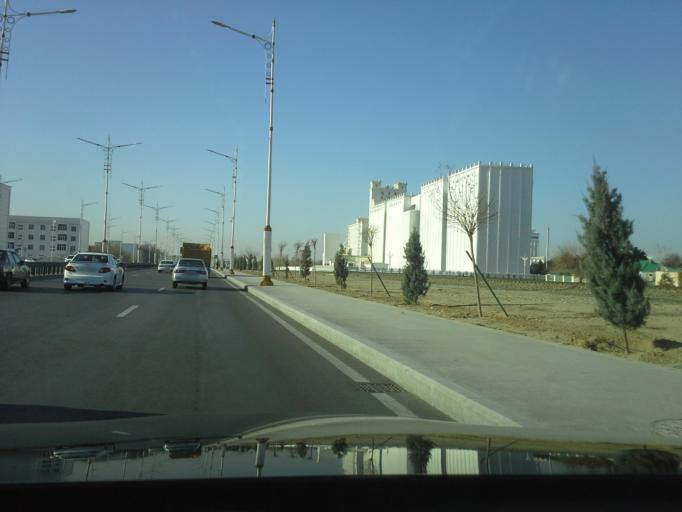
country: TM
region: Ahal
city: Ashgabat
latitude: 37.9539
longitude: 58.3757
